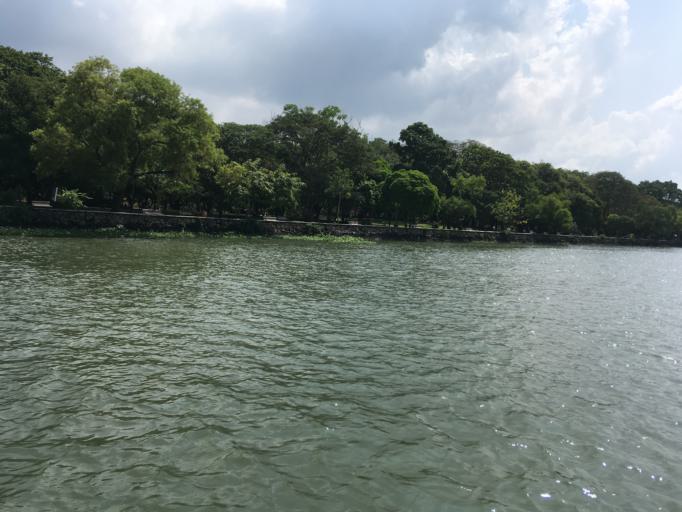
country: IN
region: Kerala
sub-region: Ernakulam
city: Cochin
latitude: 9.9716
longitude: 76.2784
